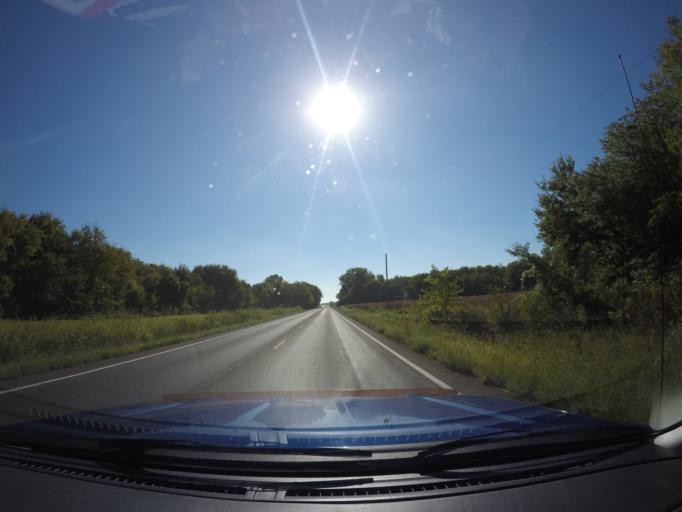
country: US
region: Kansas
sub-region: Pottawatomie County
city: Saint Marys
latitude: 39.2062
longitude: -96.0998
